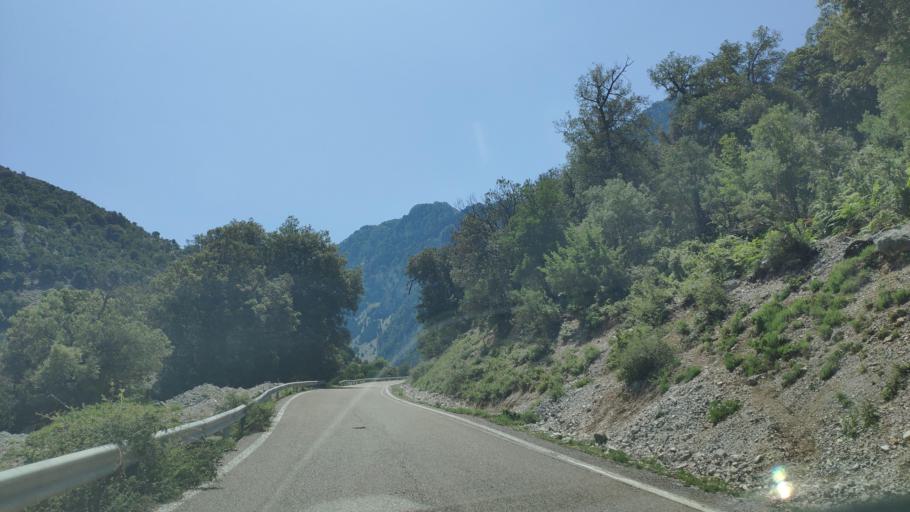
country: GR
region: West Greece
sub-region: Nomos Aitolias kai Akarnanias
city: Krikellos
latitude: 39.0135
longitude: 21.3567
